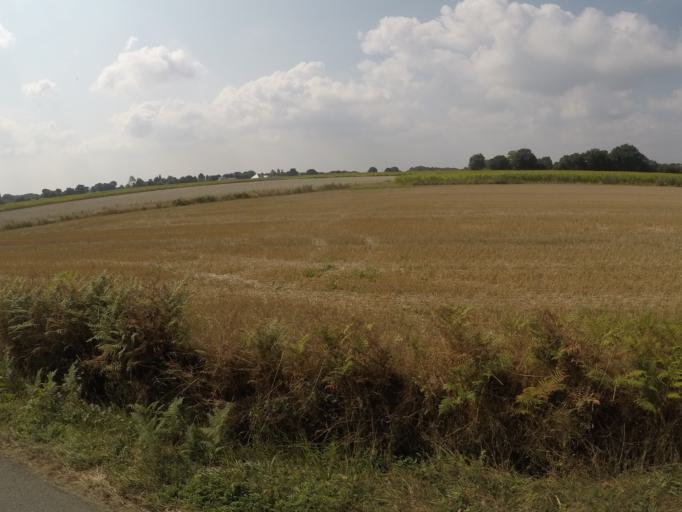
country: FR
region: Brittany
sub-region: Departement des Cotes-d'Armor
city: Tremuson
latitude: 48.5337
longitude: -2.8926
